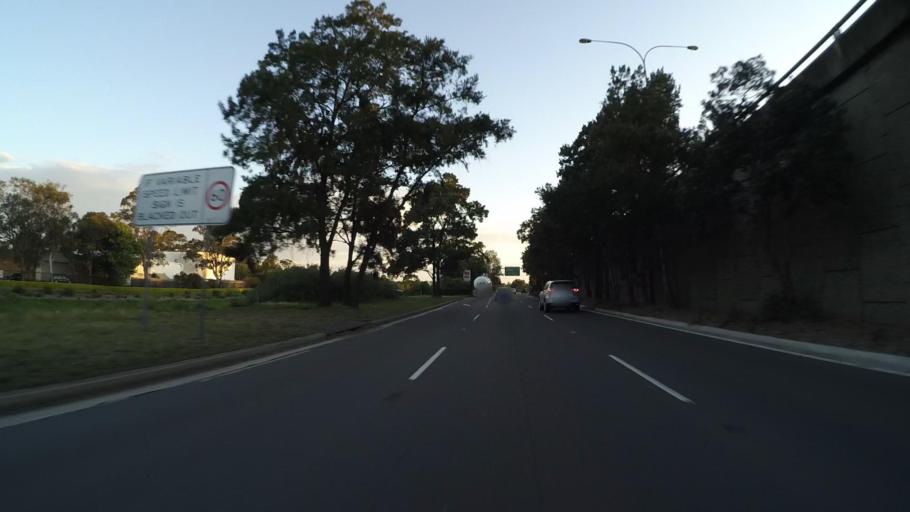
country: AU
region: New South Wales
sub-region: Botany Bay
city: Botany
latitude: -33.9406
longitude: 151.1928
